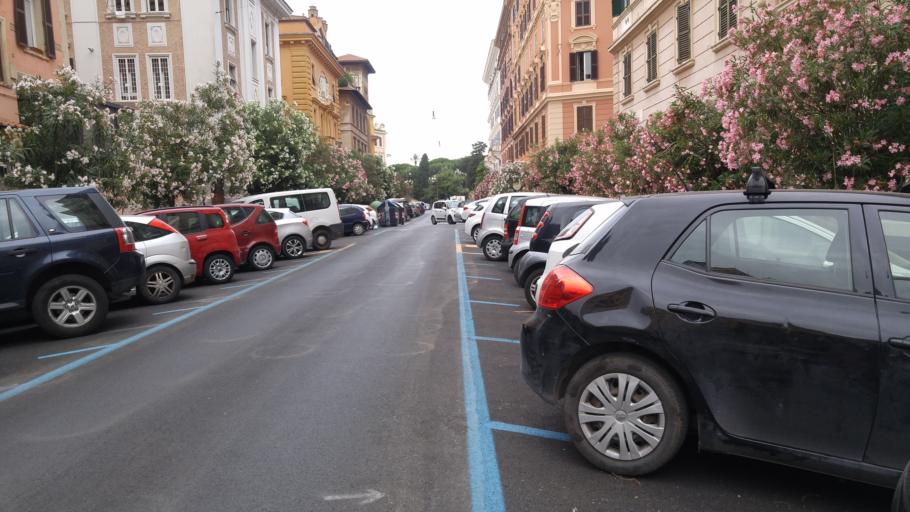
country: IT
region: Latium
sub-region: Citta metropolitana di Roma Capitale
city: Rome
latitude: 41.8906
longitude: 12.5000
